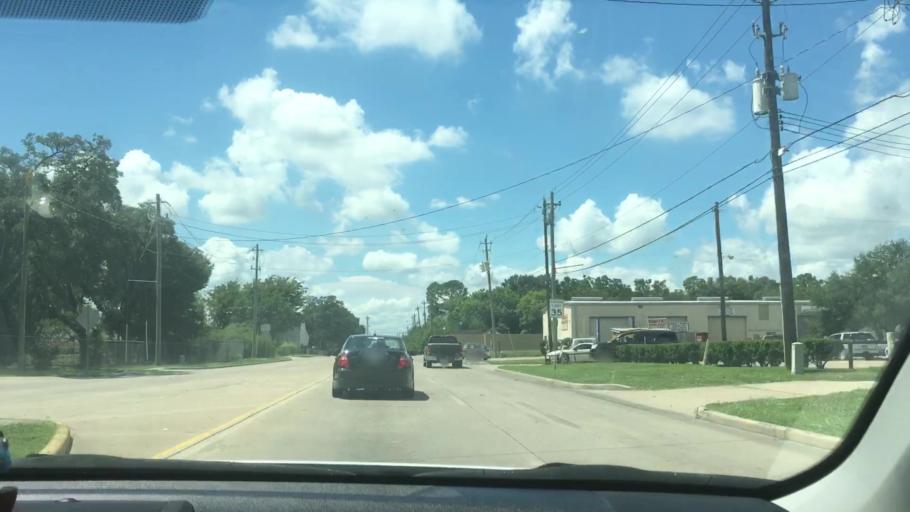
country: US
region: Texas
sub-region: Fort Bend County
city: Fifth Street
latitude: 29.6042
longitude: -95.5493
